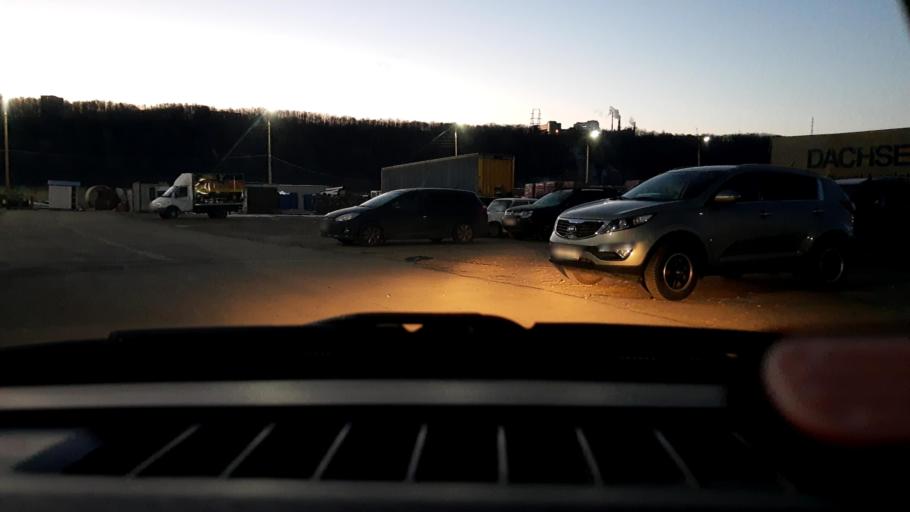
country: RU
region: Nizjnij Novgorod
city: Nizhniy Novgorod
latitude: 56.2474
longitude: 43.9338
